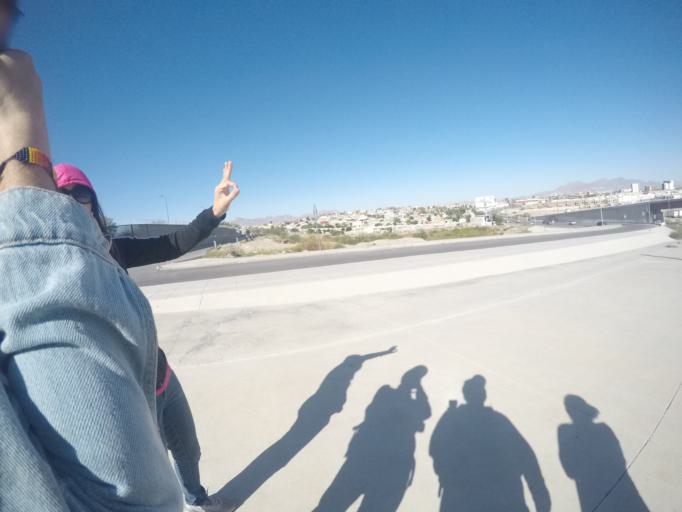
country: US
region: Texas
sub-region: El Paso County
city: Socorro
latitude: 31.6699
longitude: -106.4016
